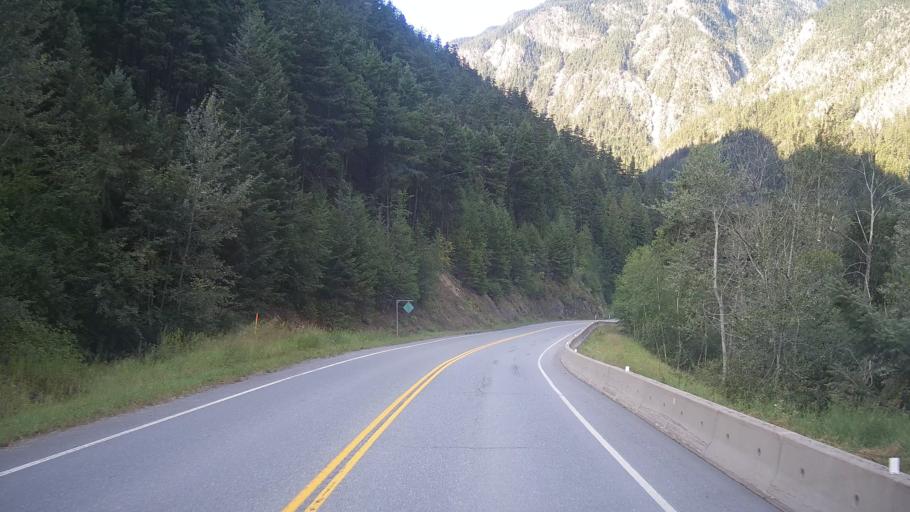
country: CA
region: British Columbia
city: Lillooet
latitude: 50.6280
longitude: -122.0951
